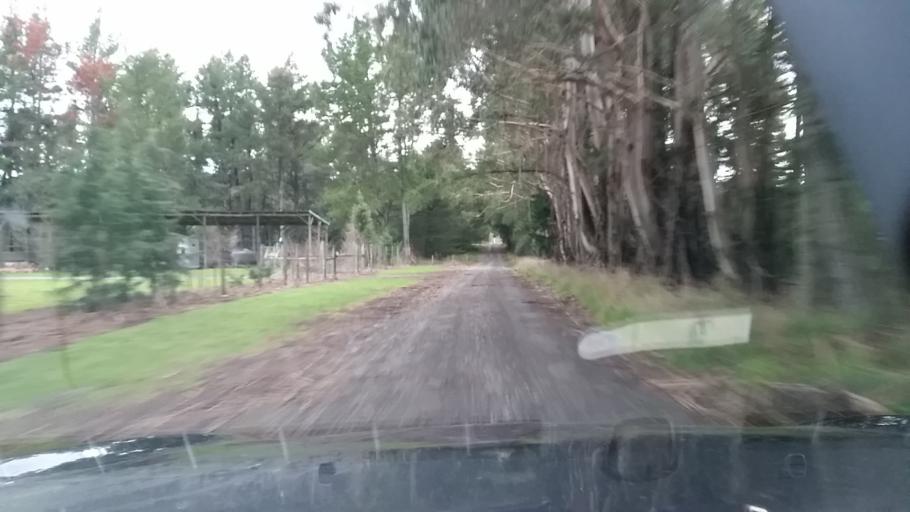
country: NZ
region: Marlborough
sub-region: Marlborough District
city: Blenheim
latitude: -41.5356
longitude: 173.6136
